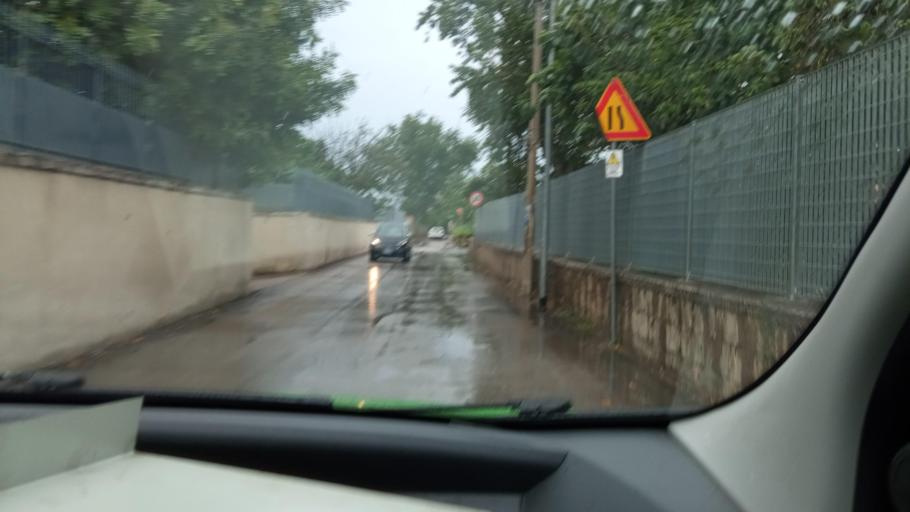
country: IT
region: Campania
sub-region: Provincia di Napoli
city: Pozzuoli
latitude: 40.8406
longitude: 14.1176
